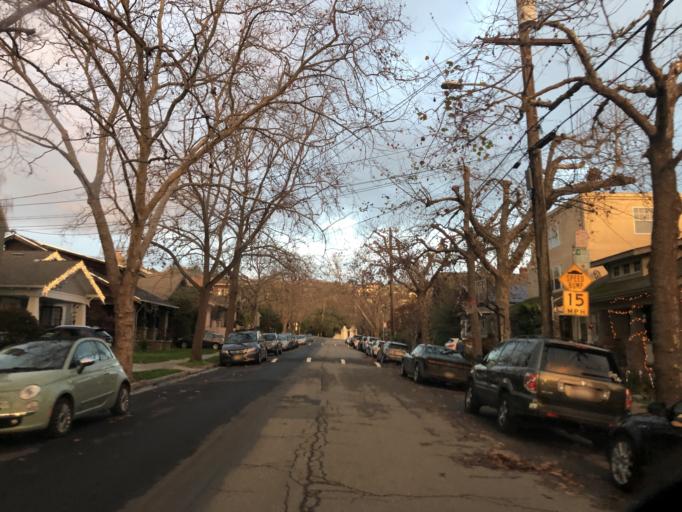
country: US
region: California
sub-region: Alameda County
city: Piedmont
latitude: 37.8445
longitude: -122.2467
